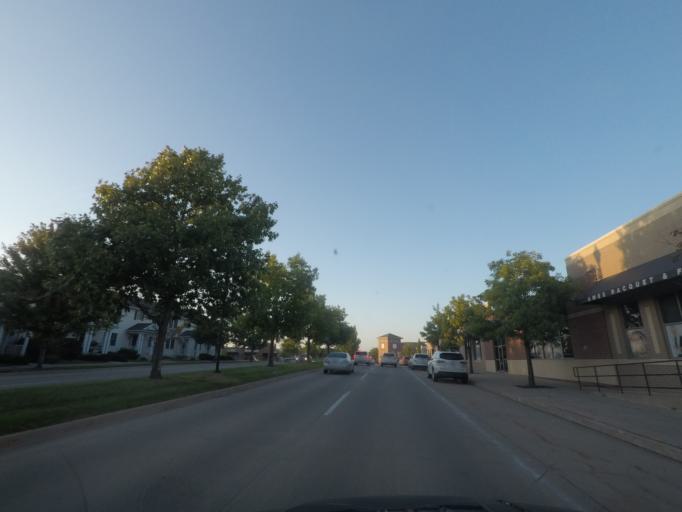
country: US
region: Iowa
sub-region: Story County
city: Ames
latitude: 42.0478
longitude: -93.6448
